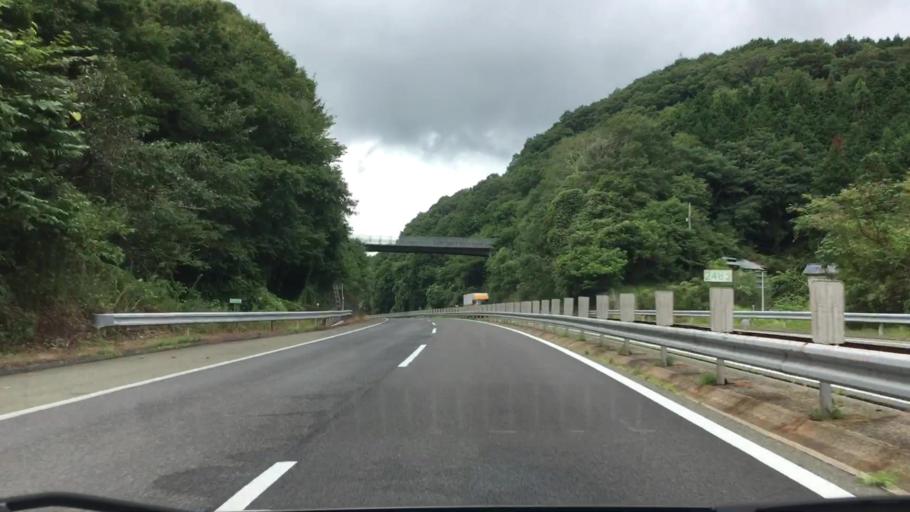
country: JP
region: Okayama
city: Niimi
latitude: 34.8896
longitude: 133.2641
